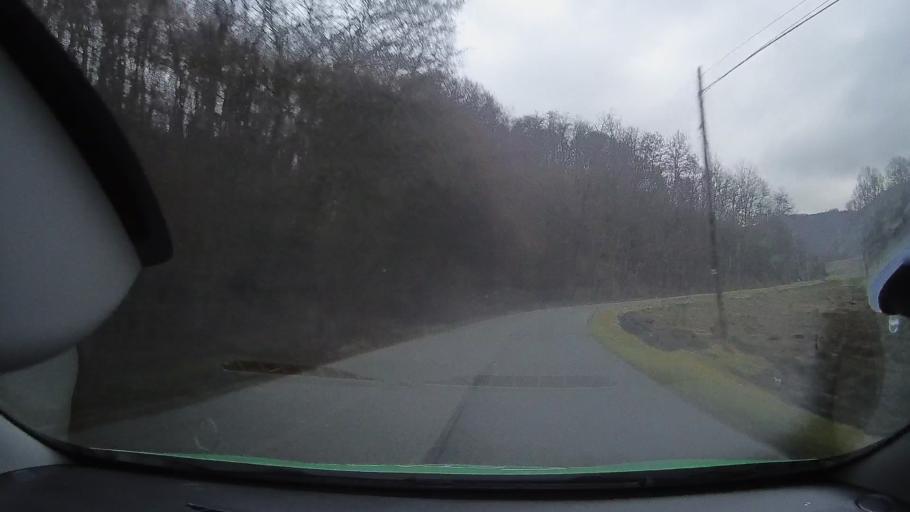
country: RO
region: Hunedoara
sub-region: Comuna Baia de Cris
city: Baia de Cris
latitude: 46.1987
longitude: 22.7179
